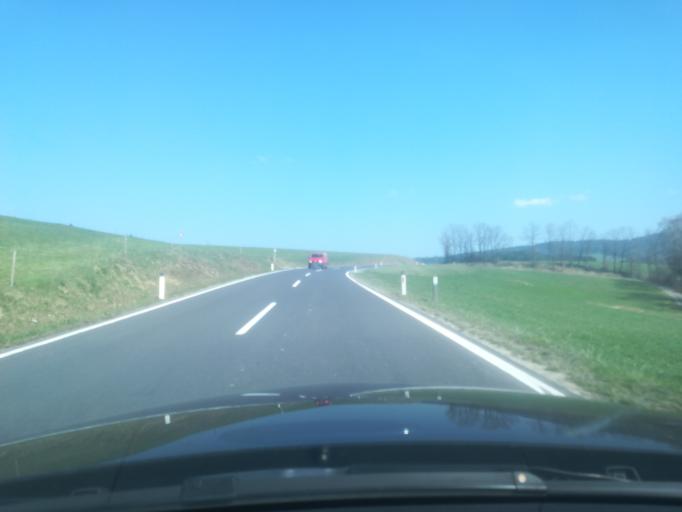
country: AT
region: Upper Austria
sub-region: Politischer Bezirk Perg
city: Perg
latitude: 48.3558
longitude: 14.6782
